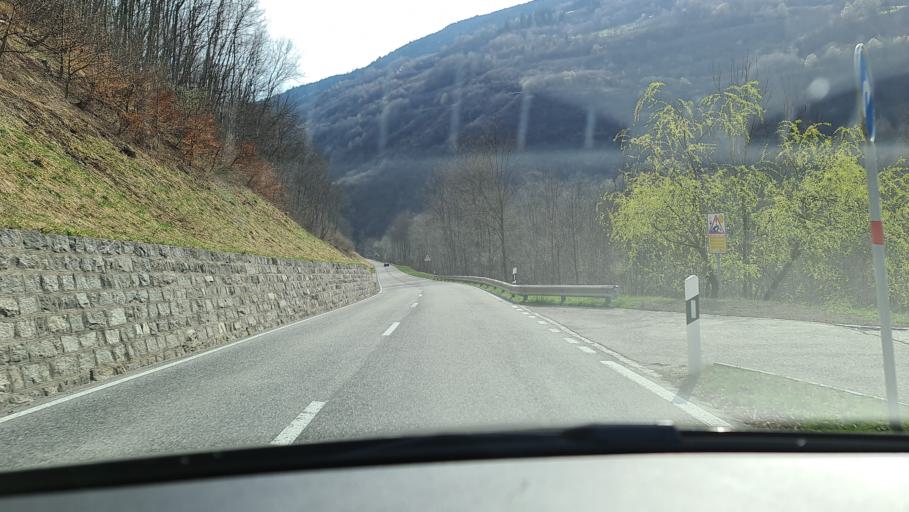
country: CH
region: Ticino
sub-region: Blenio District
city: Acquarossa
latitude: 46.5241
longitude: 8.9405
